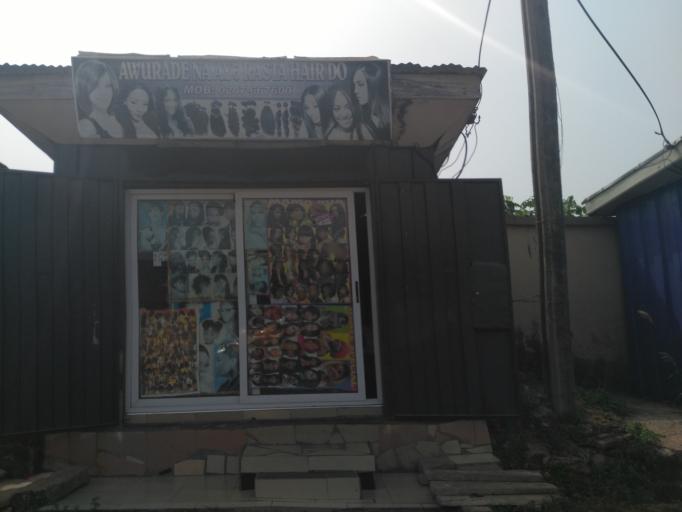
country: GH
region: Ashanti
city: Kumasi
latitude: 6.6811
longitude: -1.6022
